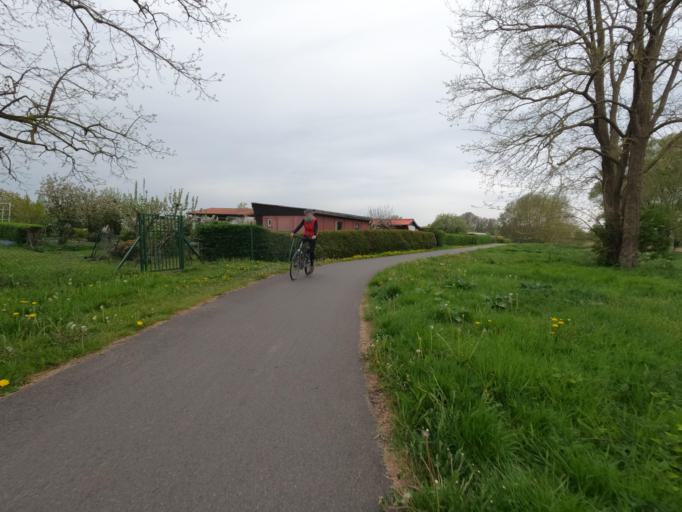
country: DE
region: Mecklenburg-Vorpommern
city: Ribnitz-Damgarten
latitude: 54.2497
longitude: 12.4025
